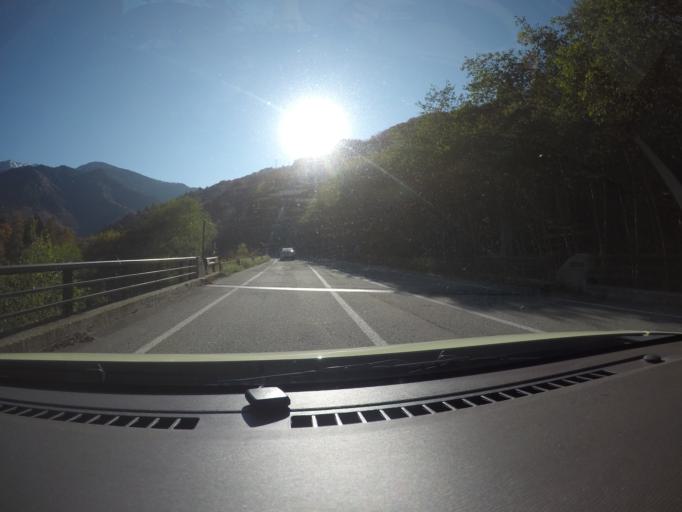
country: JP
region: Gifu
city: Takayama
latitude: 36.1944
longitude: 137.5488
